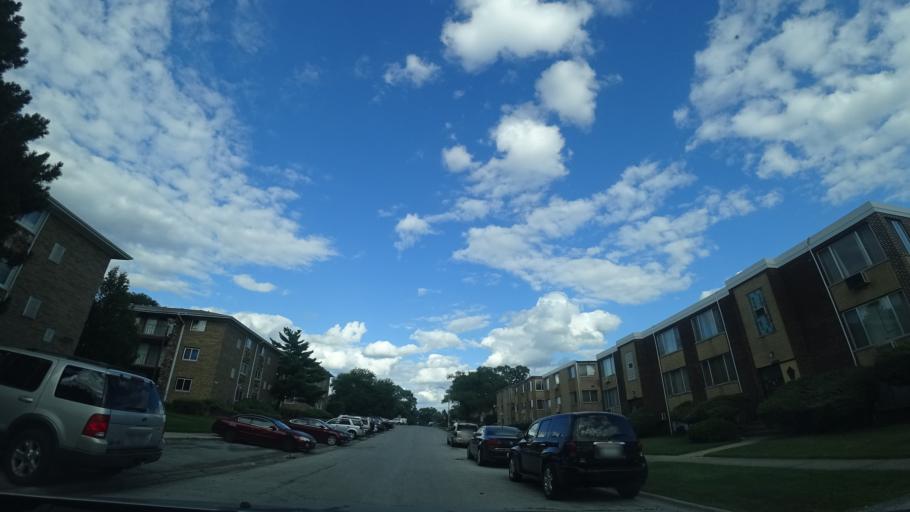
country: US
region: Illinois
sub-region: Cook County
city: Merrionette Park
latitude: 41.6831
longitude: -87.7186
